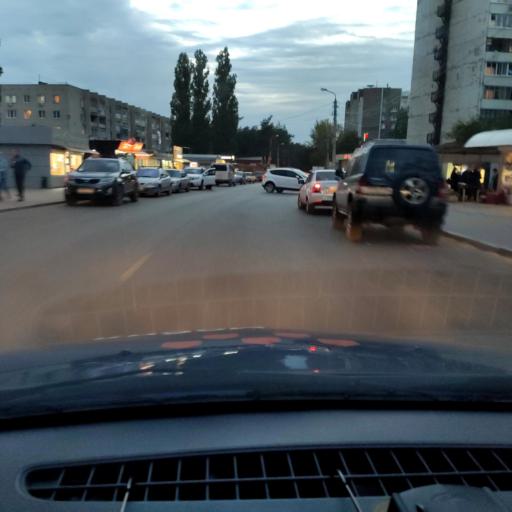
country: RU
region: Voronezj
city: Pridonskoy
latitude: 51.6825
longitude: 39.0855
